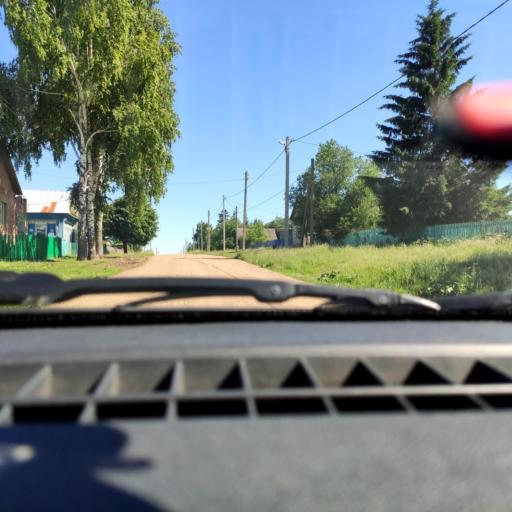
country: RU
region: Bashkortostan
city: Iglino
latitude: 54.8958
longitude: 56.4939
